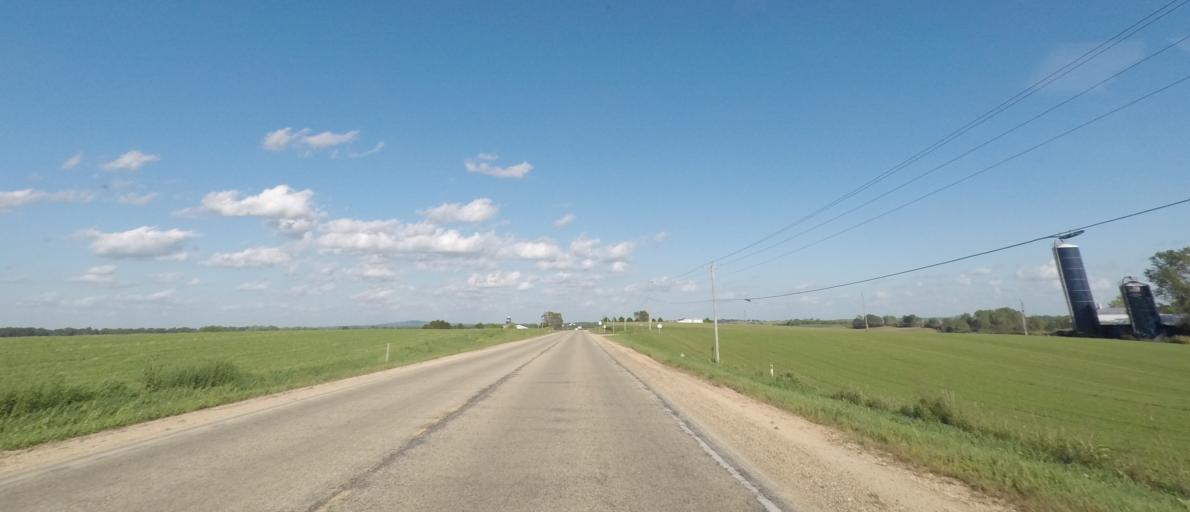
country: US
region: Wisconsin
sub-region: Iowa County
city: Dodgeville
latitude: 42.9815
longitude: -90.0980
